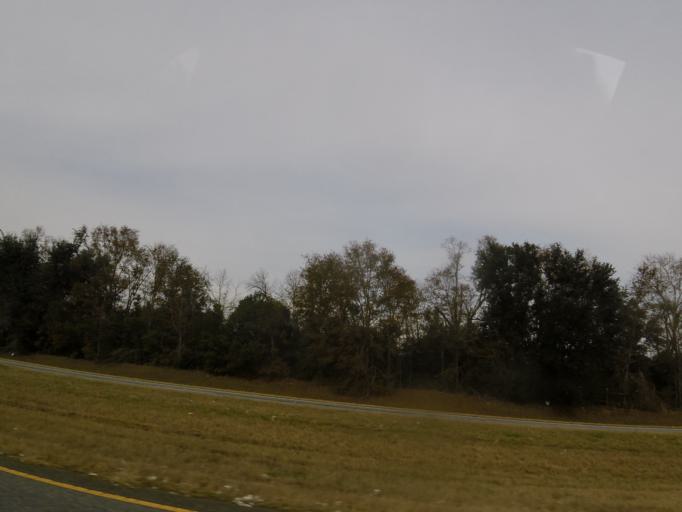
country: US
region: Georgia
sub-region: Seminole County
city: Donalsonville
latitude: 31.0102
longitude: -84.8122
